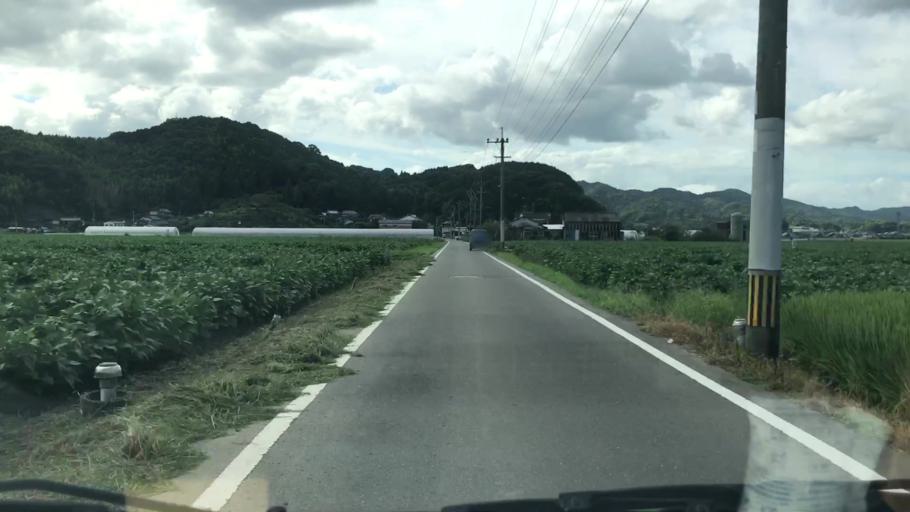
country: JP
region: Saga Prefecture
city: Kashima
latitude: 33.1161
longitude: 130.0754
